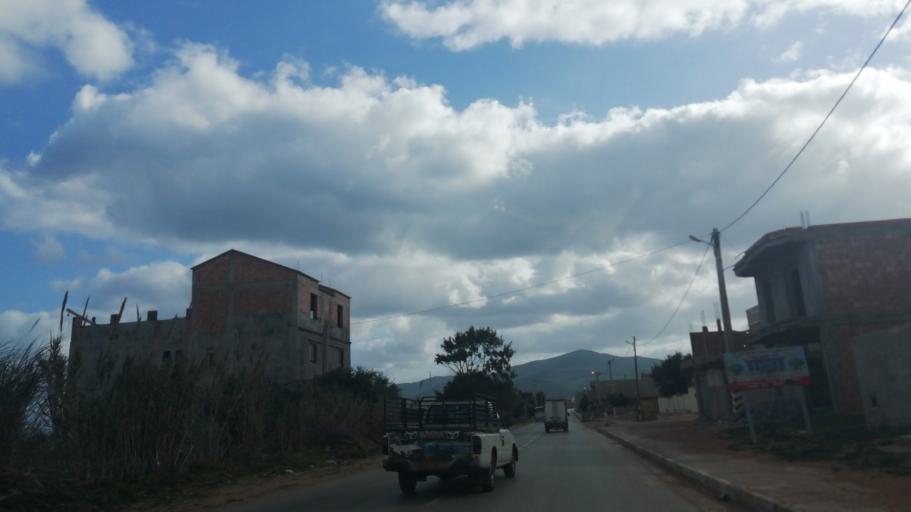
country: DZ
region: Relizane
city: Mazouna
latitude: 36.3278
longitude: 0.7226
